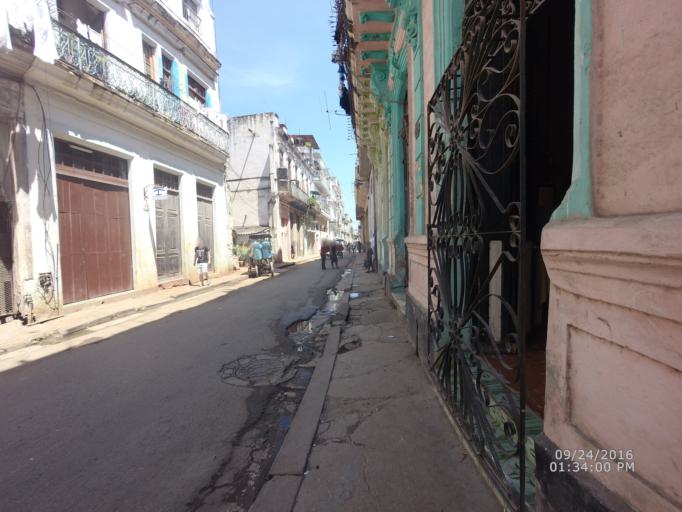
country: CU
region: La Habana
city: La Habana Vieja
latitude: 23.1340
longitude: -82.3529
